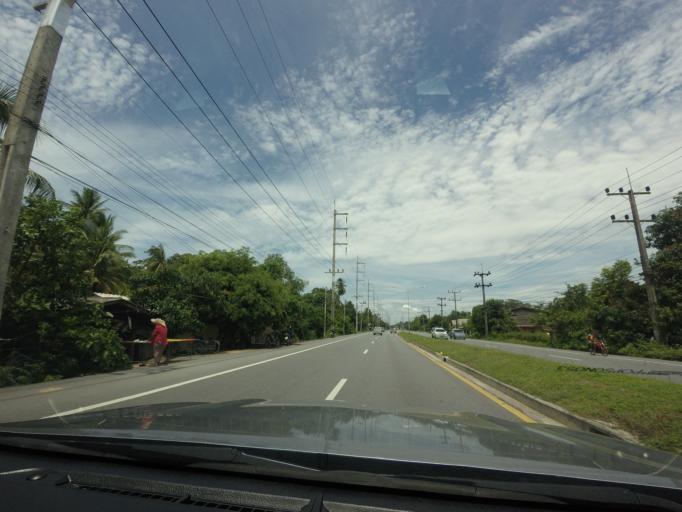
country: TH
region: Songkhla
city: Krasae Sin
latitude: 7.5856
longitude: 100.4058
